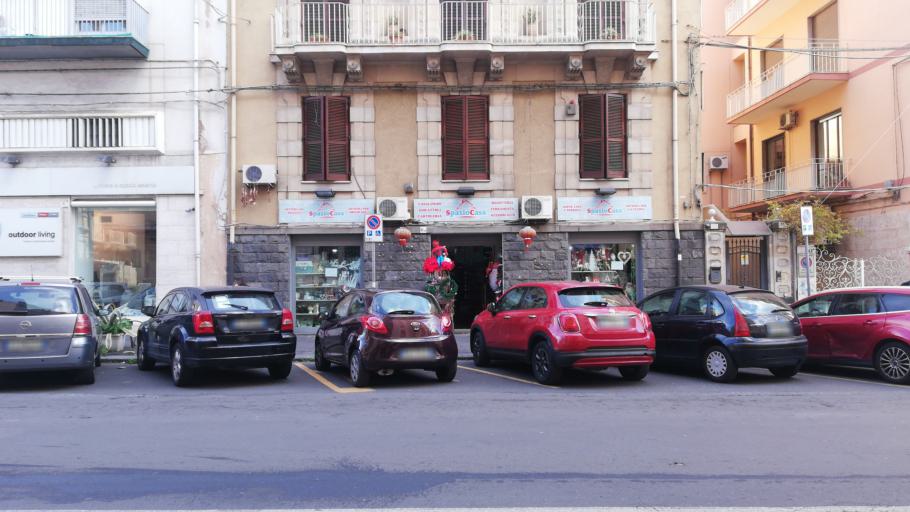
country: IT
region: Sicily
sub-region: Catania
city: Canalicchio
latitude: 37.5176
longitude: 15.0925
